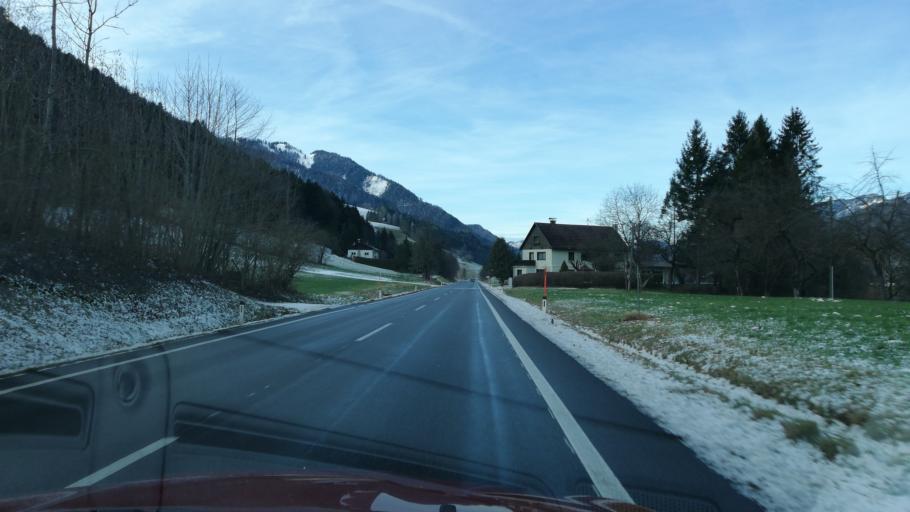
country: AT
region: Upper Austria
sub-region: Politischer Bezirk Kirchdorf an der Krems
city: Rossleithen
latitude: 47.7335
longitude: 14.2860
